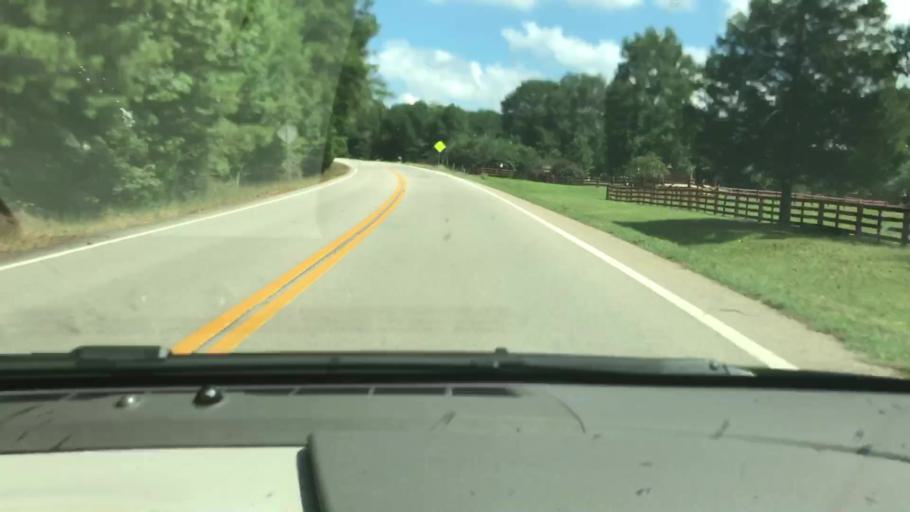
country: US
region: Georgia
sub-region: Troup County
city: La Grange
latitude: 32.9490
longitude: -85.0180
